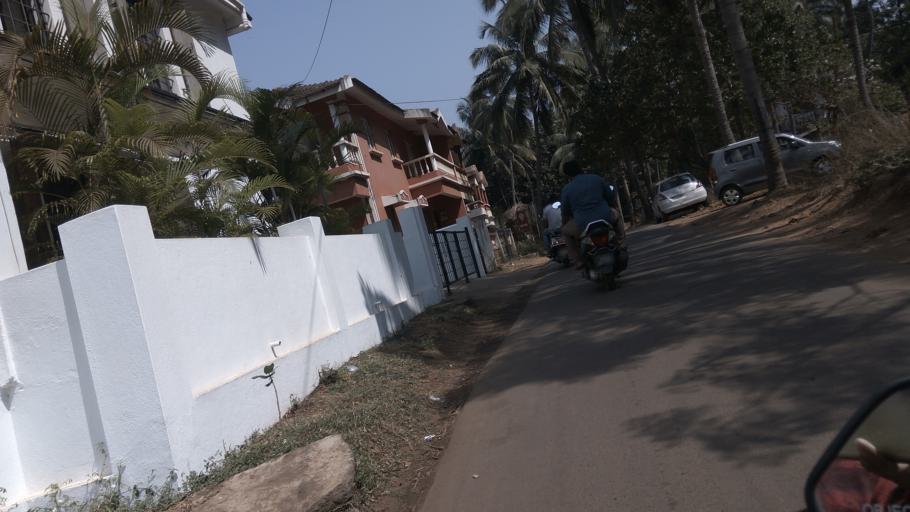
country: IN
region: Goa
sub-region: North Goa
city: Candolim
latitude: 15.5227
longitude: 73.7670
